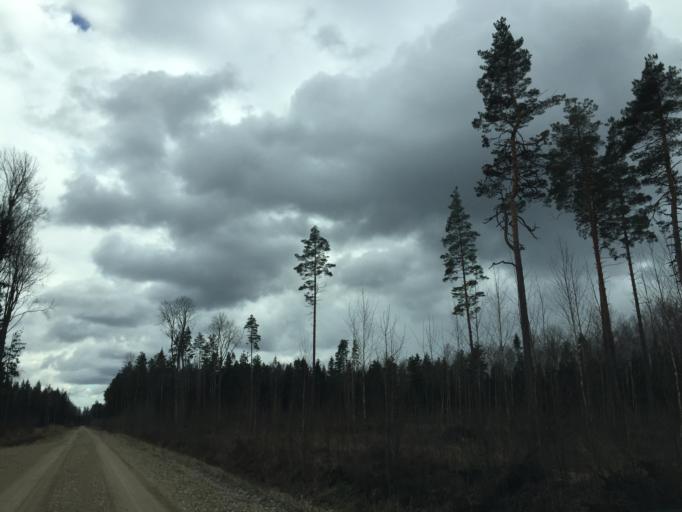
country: LV
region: Akniste
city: Akniste
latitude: 56.0860
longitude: 25.7617
